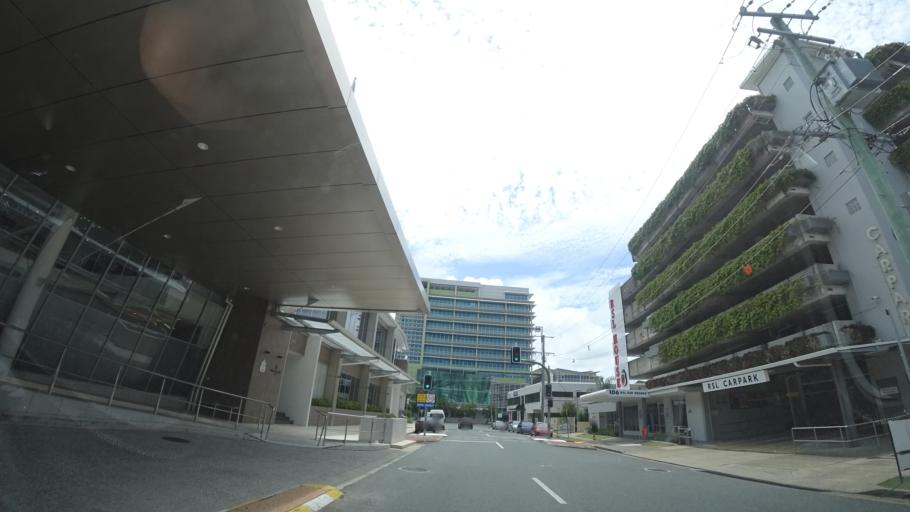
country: AU
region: Queensland
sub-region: Sunshine Coast
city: Mooloolaba
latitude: -26.6554
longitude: 153.0942
